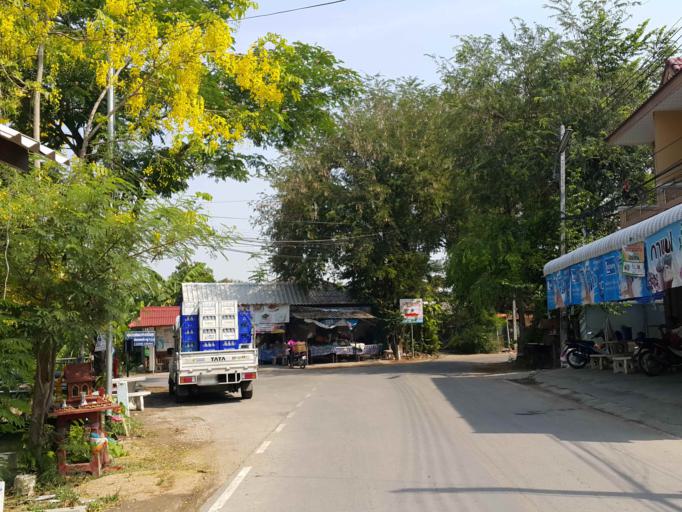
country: TH
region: Chiang Mai
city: Saraphi
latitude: 18.7497
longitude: 99.0506
